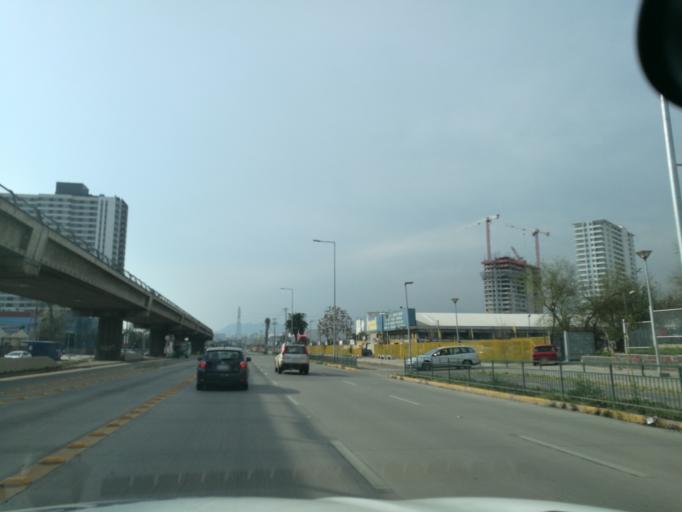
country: CL
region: Santiago Metropolitan
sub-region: Provincia de Santiago
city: Santiago
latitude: -33.4899
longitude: -70.6177
